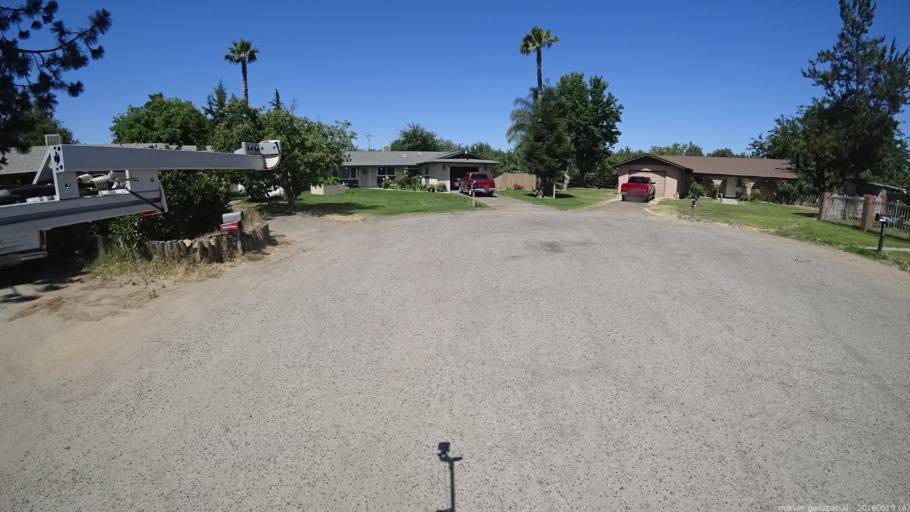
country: US
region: California
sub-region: Fresno County
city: Biola
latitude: 36.8533
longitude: -120.0566
